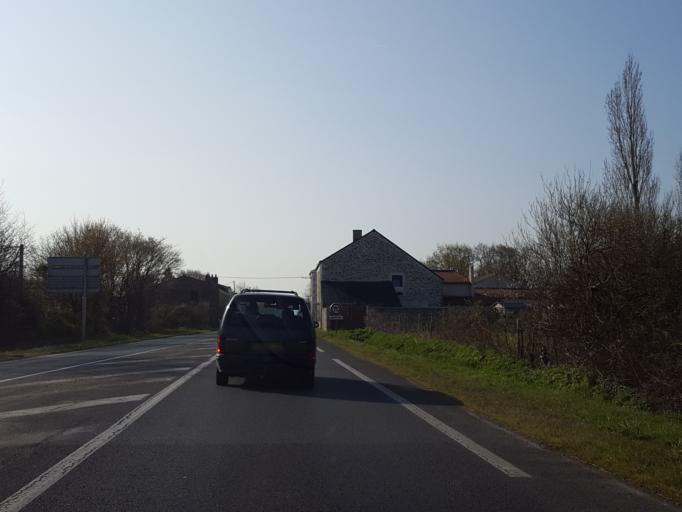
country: FR
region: Pays de la Loire
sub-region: Departement de la Loire-Atlantique
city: Le Bignon
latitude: 47.0907
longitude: -1.5296
